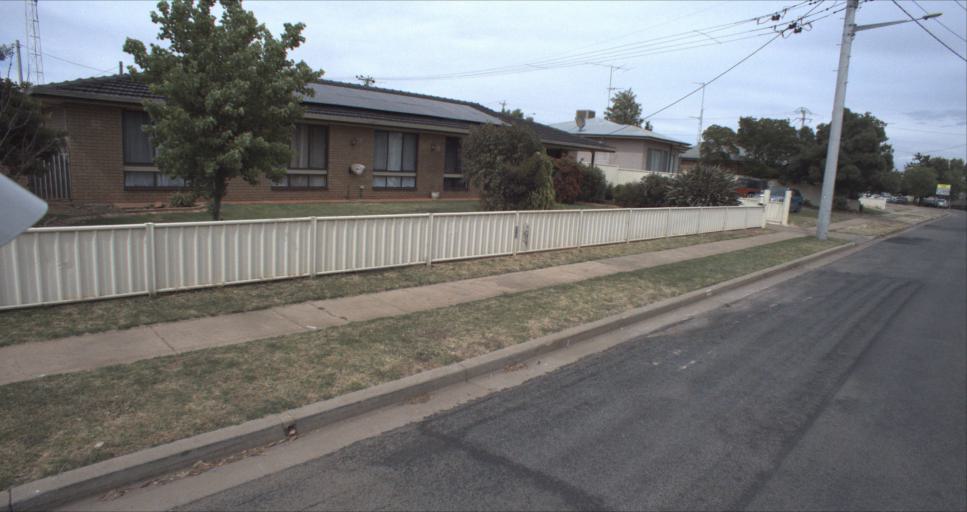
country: AU
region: New South Wales
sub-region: Leeton
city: Leeton
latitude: -34.5458
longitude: 146.4090
